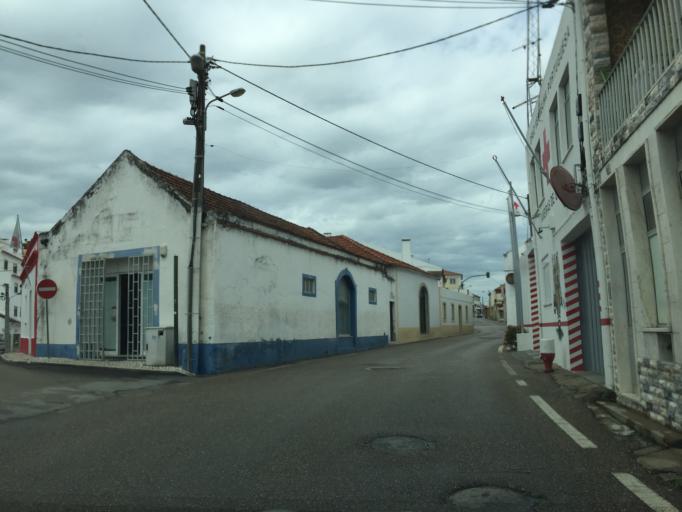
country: PT
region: Lisbon
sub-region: Azambuja
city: Aveiras de Cima
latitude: 39.1369
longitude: -8.8987
